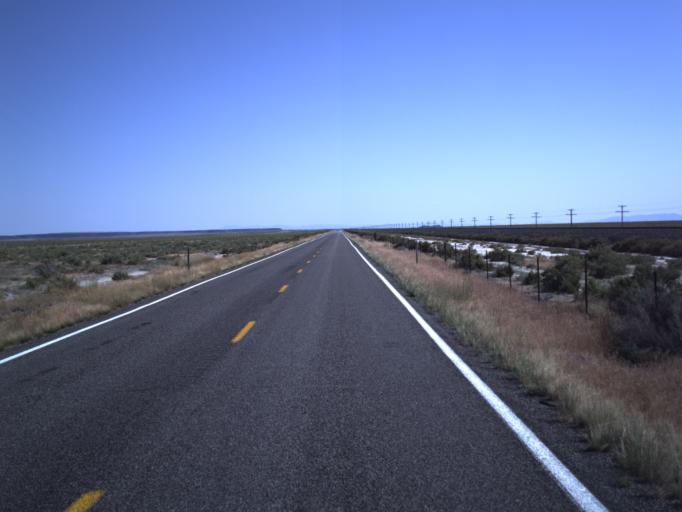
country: US
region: Utah
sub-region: Millard County
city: Delta
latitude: 39.0612
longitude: -112.7631
